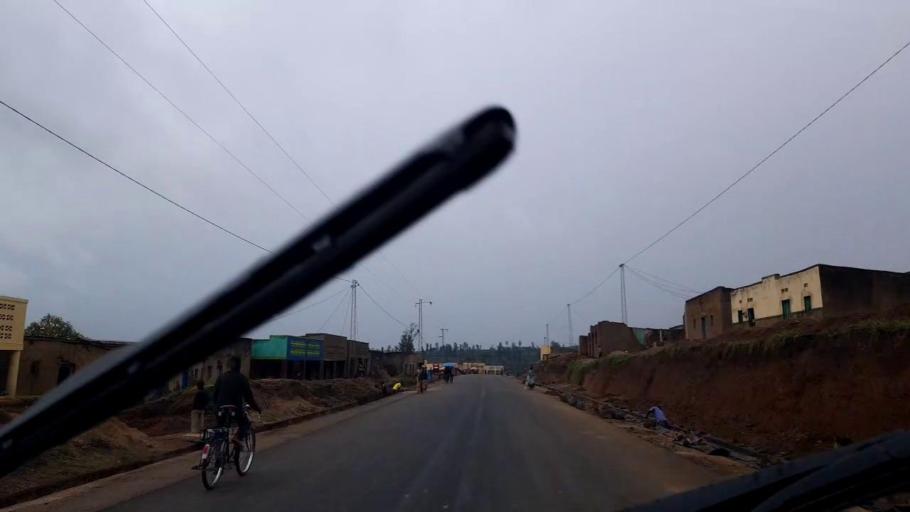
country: RW
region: Northern Province
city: Byumba
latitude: -1.4142
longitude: 30.2818
